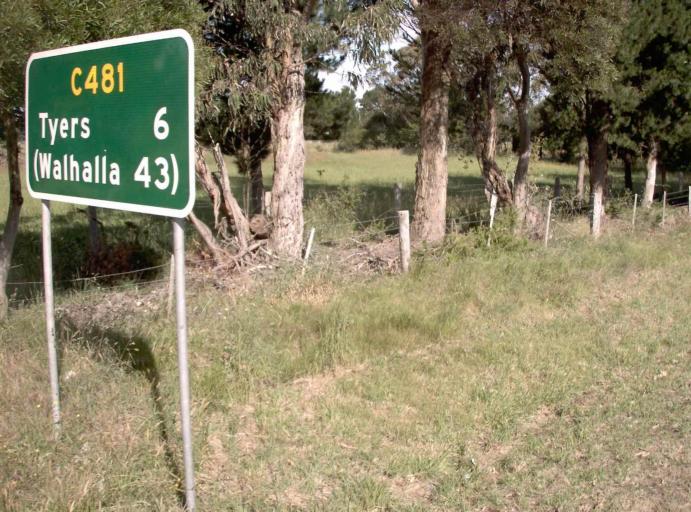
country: AU
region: Victoria
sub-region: Latrobe
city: Traralgon
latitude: -38.1890
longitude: 146.5048
